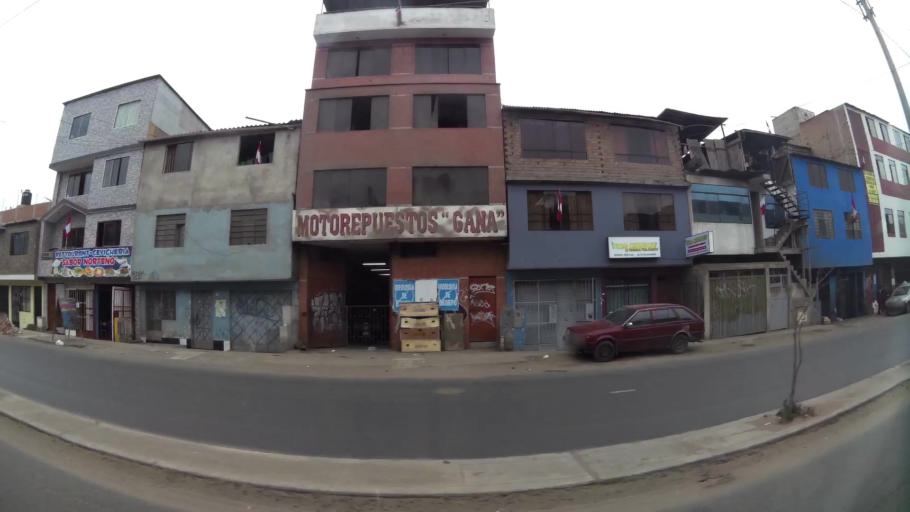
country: PE
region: Lima
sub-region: Lima
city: Surco
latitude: -12.2100
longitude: -76.9452
